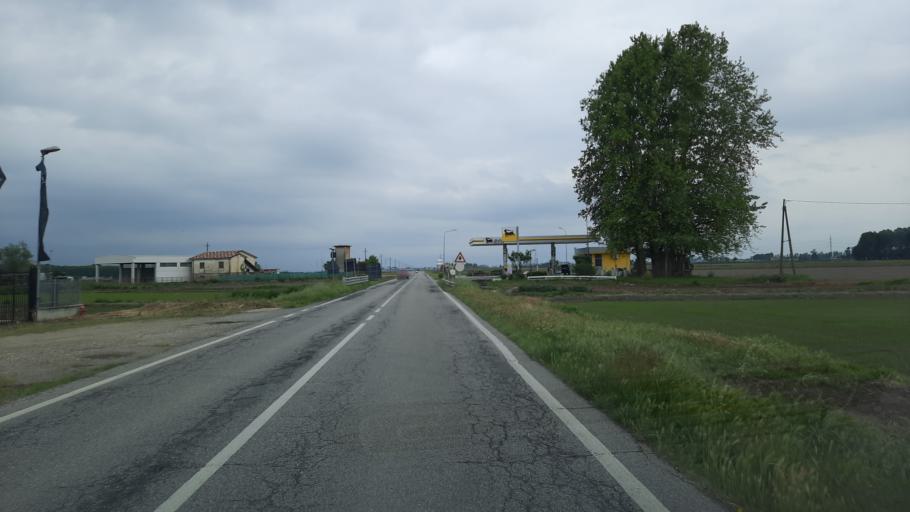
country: IT
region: Lombardy
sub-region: Provincia di Pavia
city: Robbio
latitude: 45.2804
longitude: 8.6035
